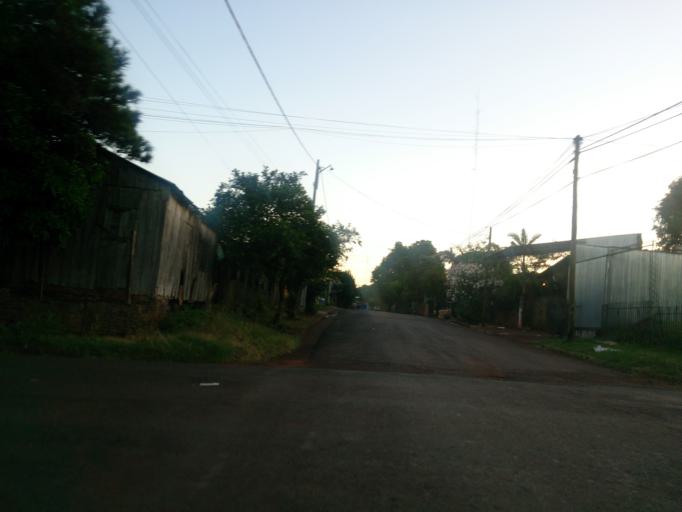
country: AR
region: Misiones
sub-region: Departamento de Obera
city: Obera
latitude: -27.4932
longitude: -55.1252
